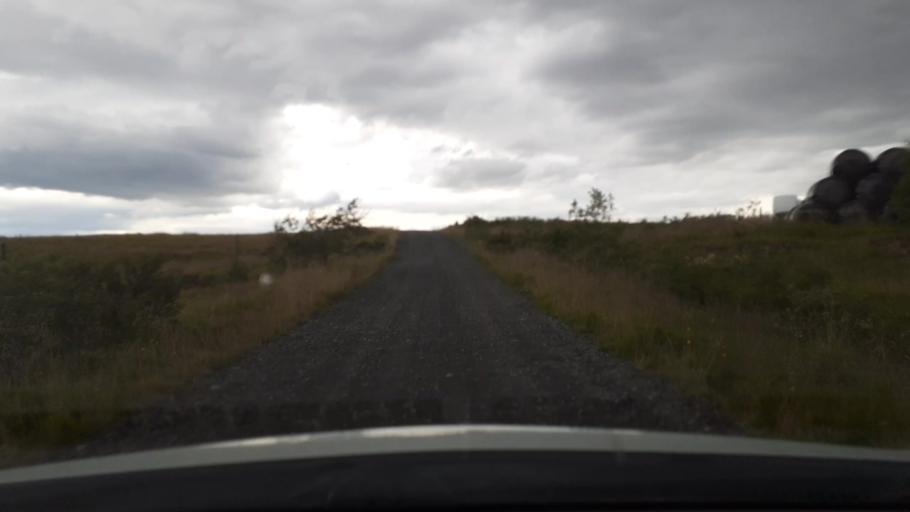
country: IS
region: West
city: Borgarnes
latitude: 64.6378
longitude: -21.7355
